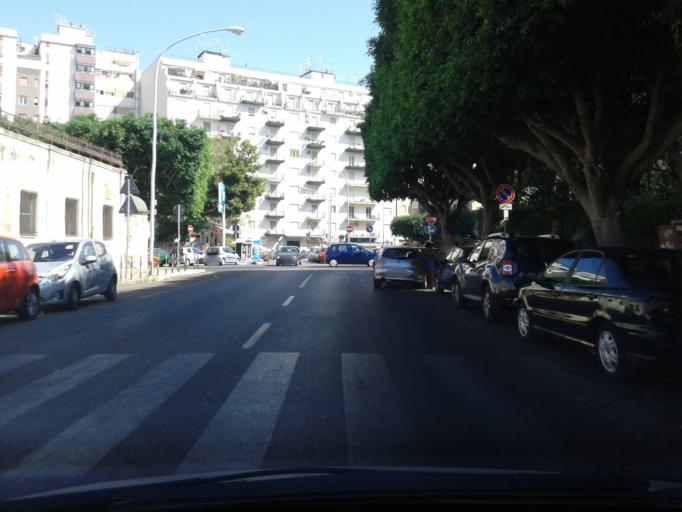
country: IT
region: Sicily
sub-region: Palermo
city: Palermo
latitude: 38.1013
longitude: 13.3379
